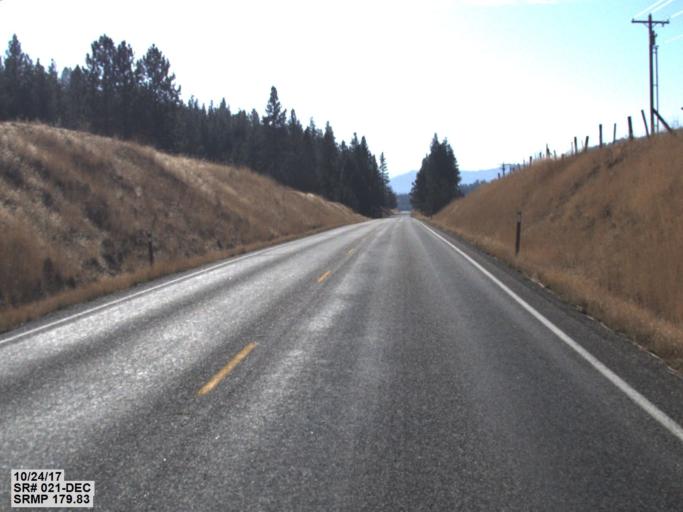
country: CA
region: British Columbia
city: Grand Forks
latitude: 48.8655
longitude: -118.6056
